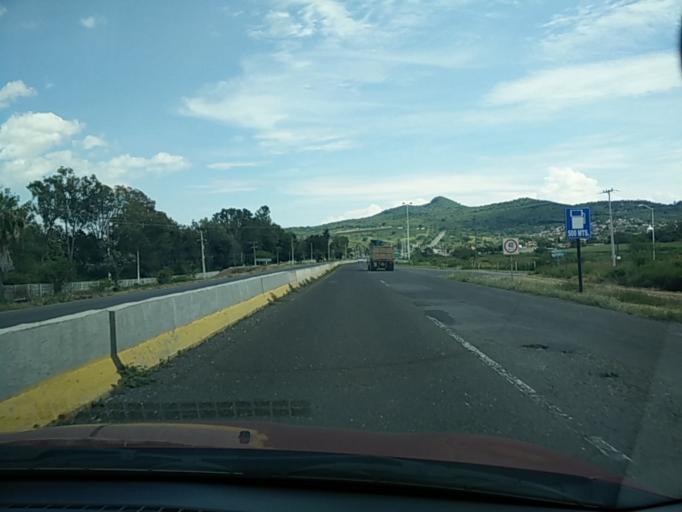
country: MX
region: Jalisco
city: Ixtlahuacan de los Membrillos
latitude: 20.3575
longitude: -103.1953
